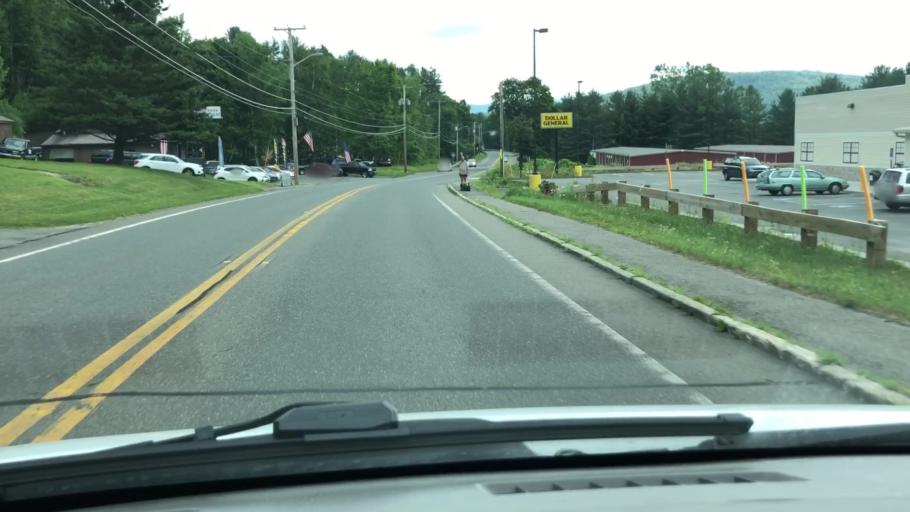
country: US
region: Massachusetts
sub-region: Berkshire County
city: Adams
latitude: 42.5669
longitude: -73.1616
